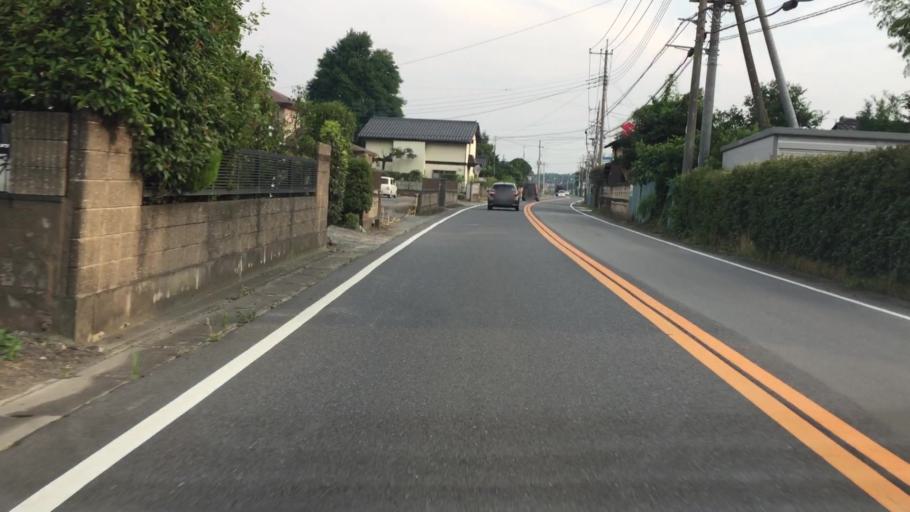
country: JP
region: Tochigi
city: Fujioka
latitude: 36.3090
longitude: 139.6722
